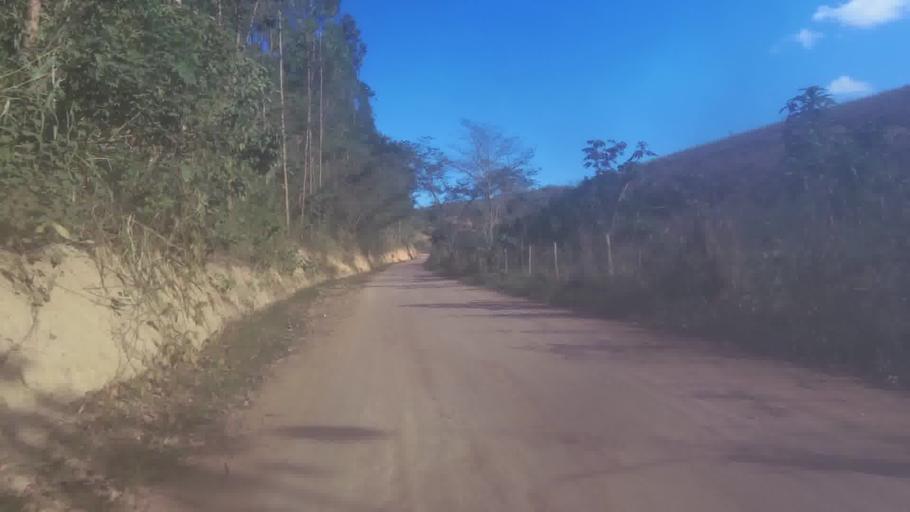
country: BR
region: Espirito Santo
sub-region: Mimoso Do Sul
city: Mimoso do Sul
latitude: -21.1001
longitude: -41.1374
